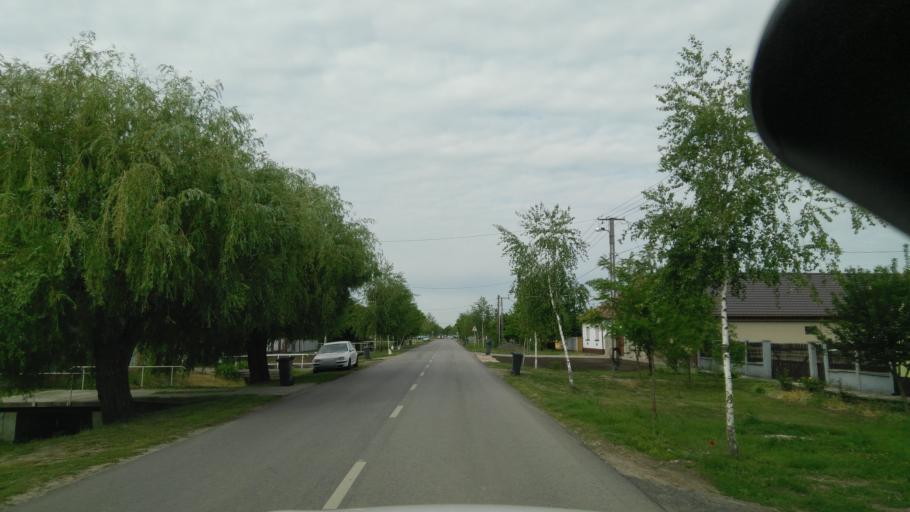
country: HU
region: Bekes
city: Ketegyhaza
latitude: 46.5526
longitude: 21.1891
